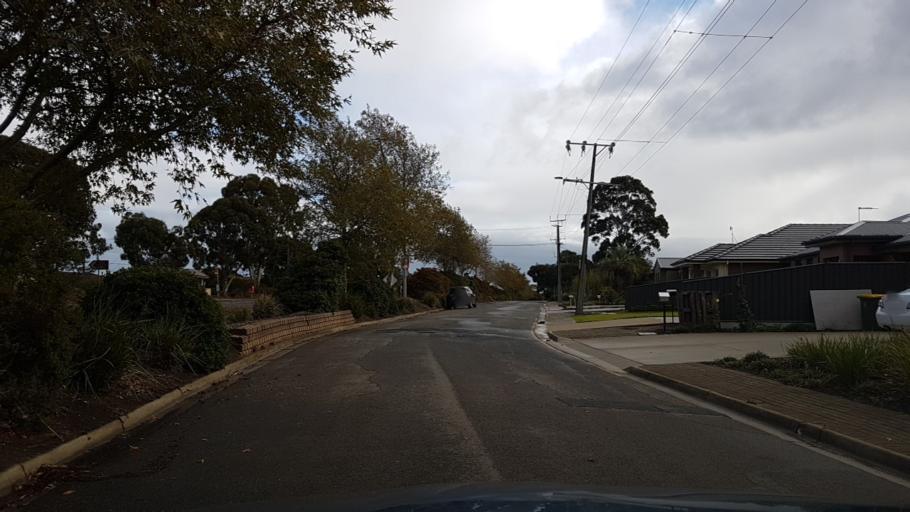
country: AU
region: South Australia
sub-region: Onkaparinga
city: Bedford Park
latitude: -35.0461
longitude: 138.5711
